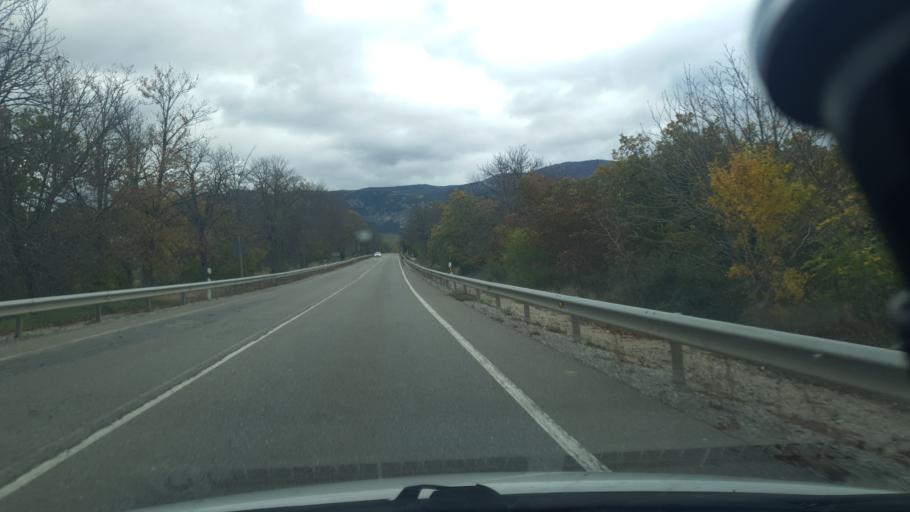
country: ES
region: Castille and Leon
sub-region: Provincia de Segovia
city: San Ildefonso
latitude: 40.9041
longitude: -4.0267
